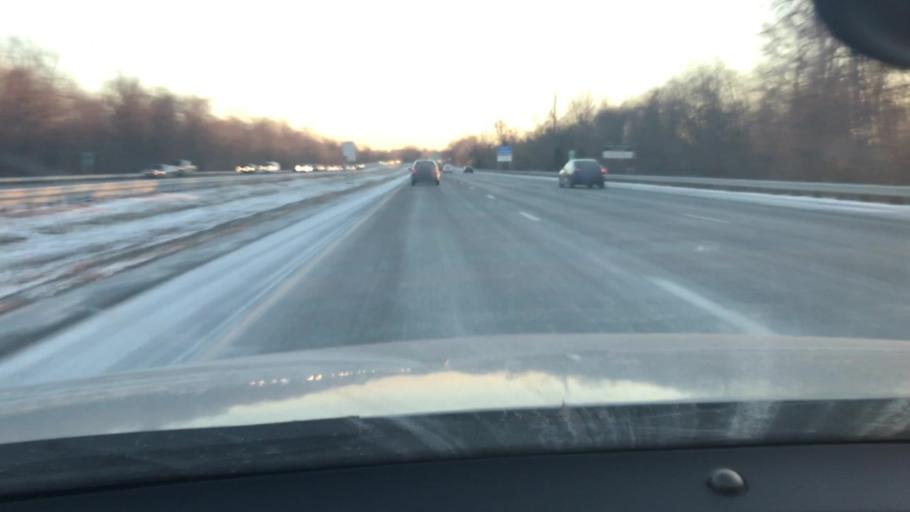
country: US
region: New Jersey
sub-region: Burlington County
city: Bordentown
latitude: 40.1668
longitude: -74.7211
